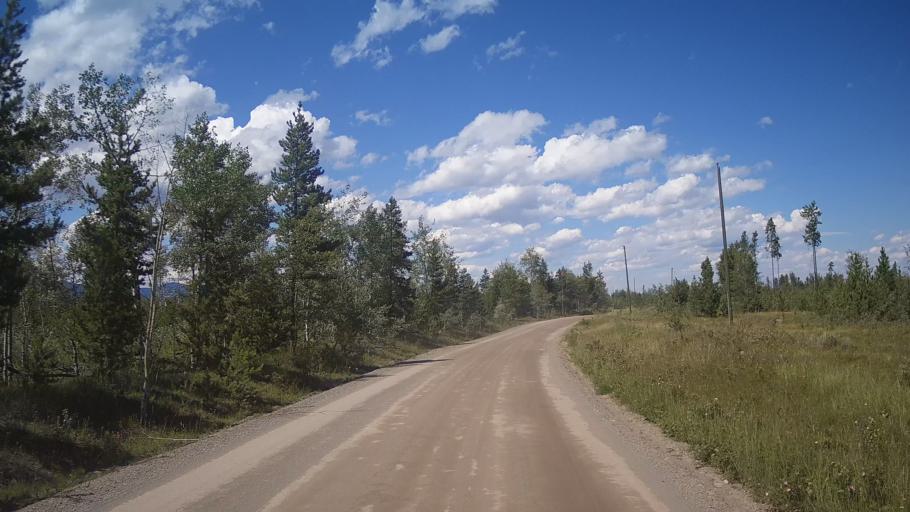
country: CA
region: British Columbia
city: Cache Creek
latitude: 51.2519
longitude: -121.6725
